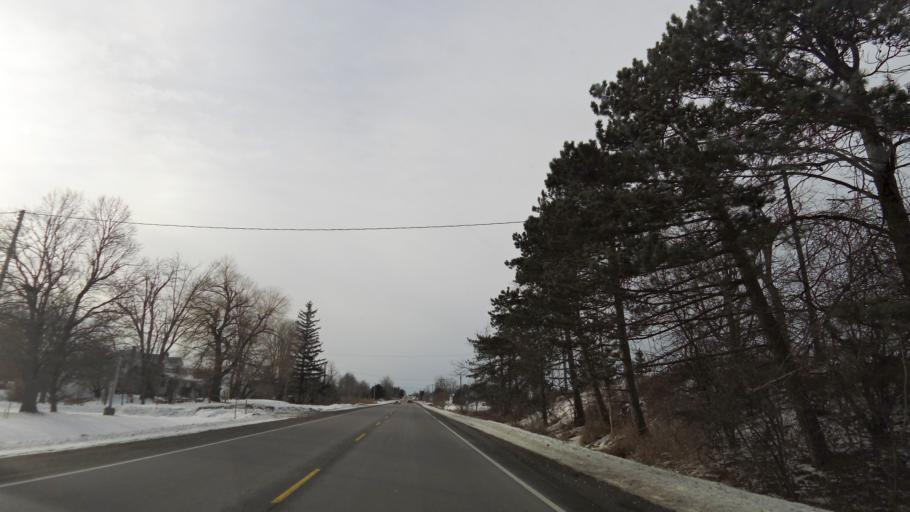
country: CA
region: Ontario
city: Ancaster
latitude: 43.2983
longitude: -79.9665
